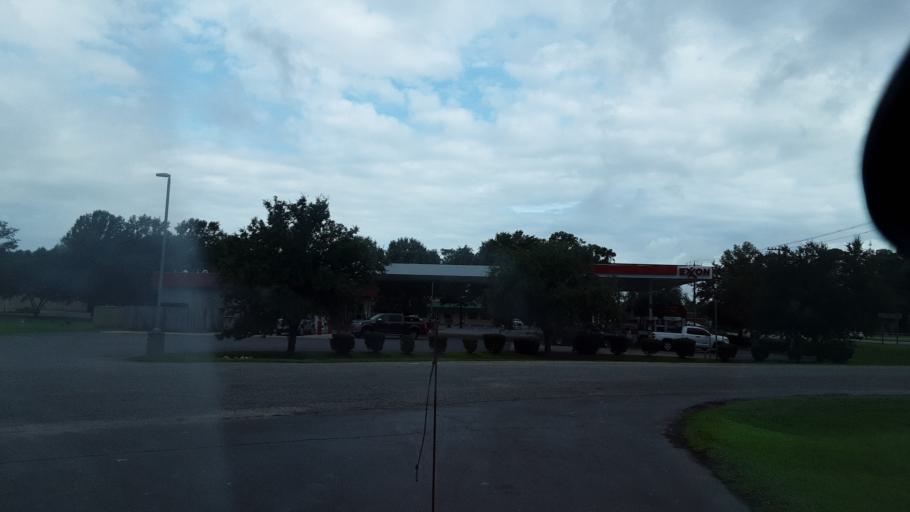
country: US
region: North Carolina
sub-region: Dare County
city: Southern Shores
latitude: 36.2392
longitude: -75.8762
